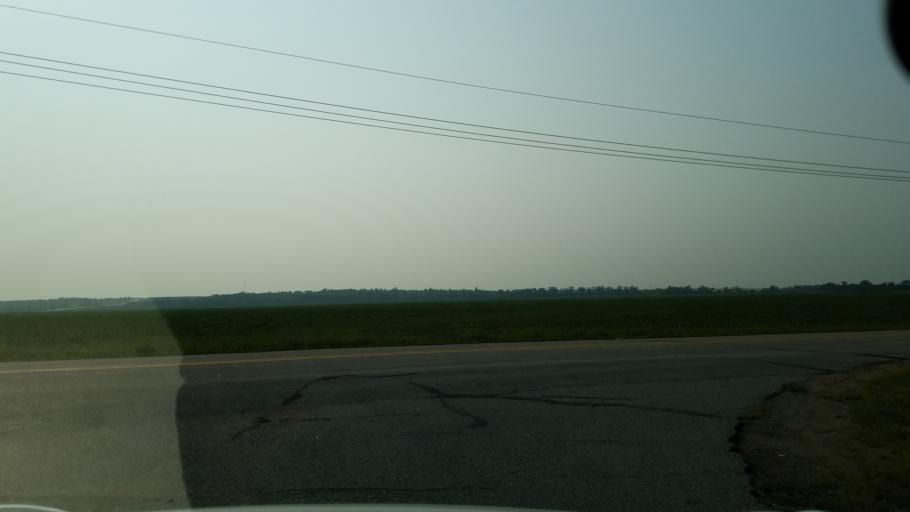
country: US
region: Nebraska
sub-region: Sarpy County
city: Offutt Air Force Base
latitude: 41.0833
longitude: -95.8896
